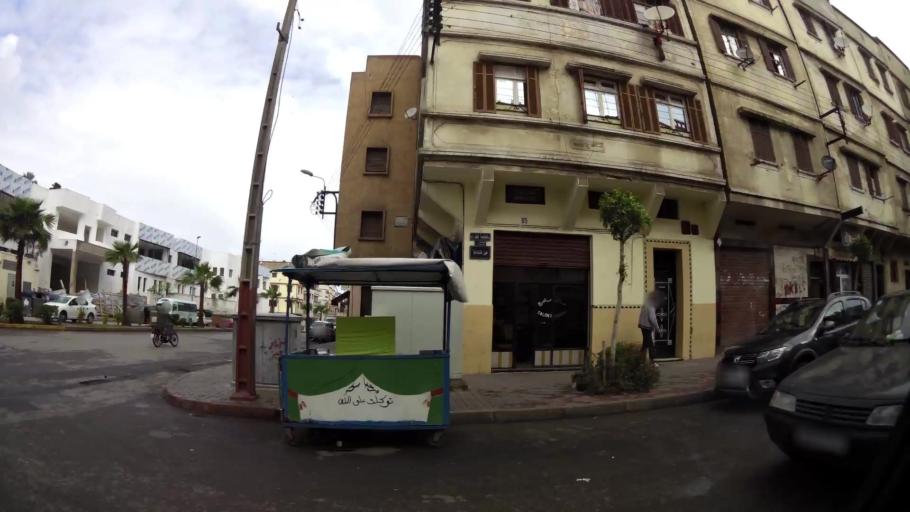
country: MA
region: Grand Casablanca
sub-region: Casablanca
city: Casablanca
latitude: 33.5697
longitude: -7.5854
